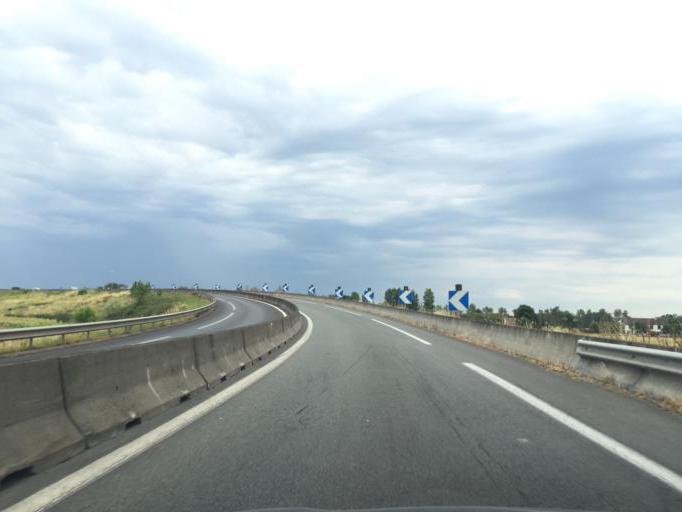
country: FR
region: Auvergne
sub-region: Departement de l'Allier
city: Toulon-sur-Allier
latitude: 46.5038
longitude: 3.3567
